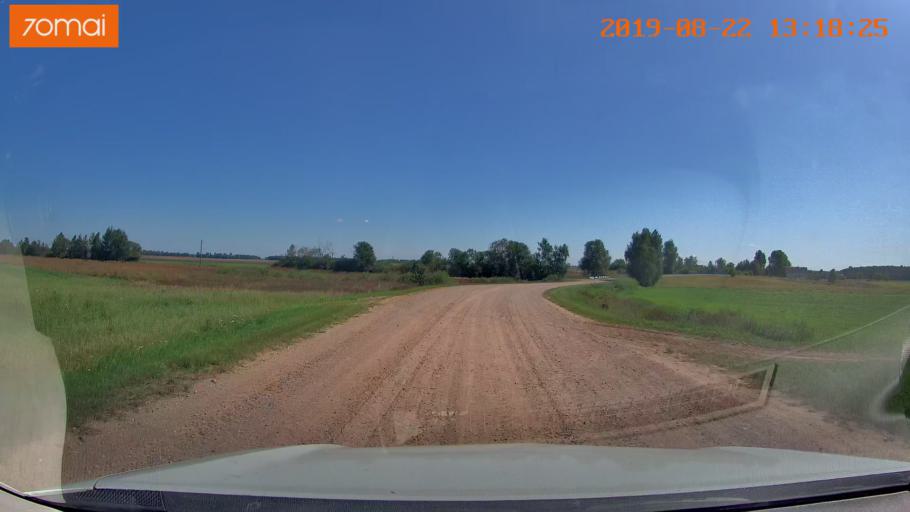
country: BY
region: Minsk
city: Urechcha
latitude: 53.2410
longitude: 27.9395
